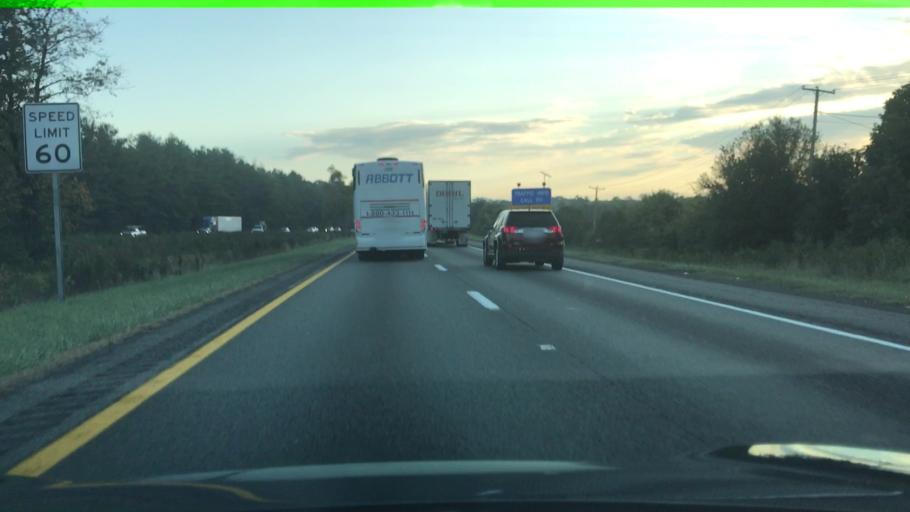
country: US
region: Virginia
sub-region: City of Salem
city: Salem
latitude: 37.3316
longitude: -80.0239
